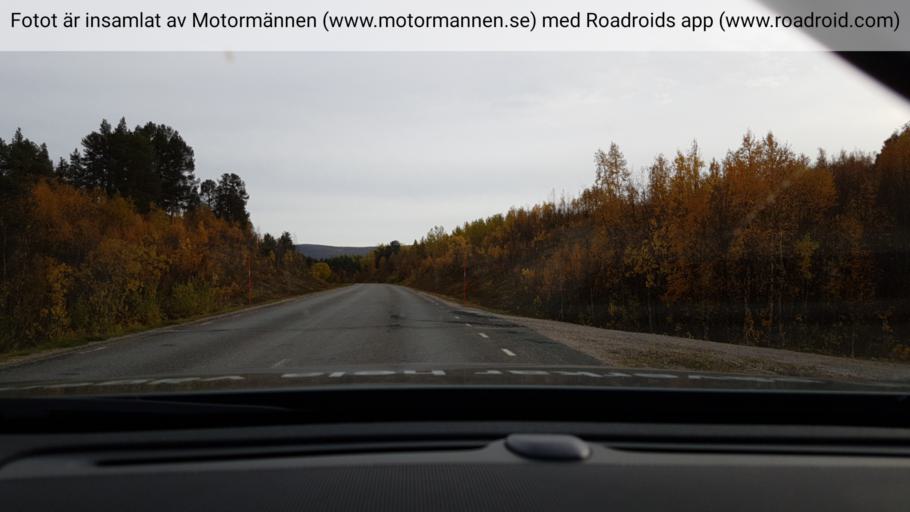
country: SE
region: Norrbotten
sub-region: Arjeplogs Kommun
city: Arjeplog
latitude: 66.4010
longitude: 16.9466
